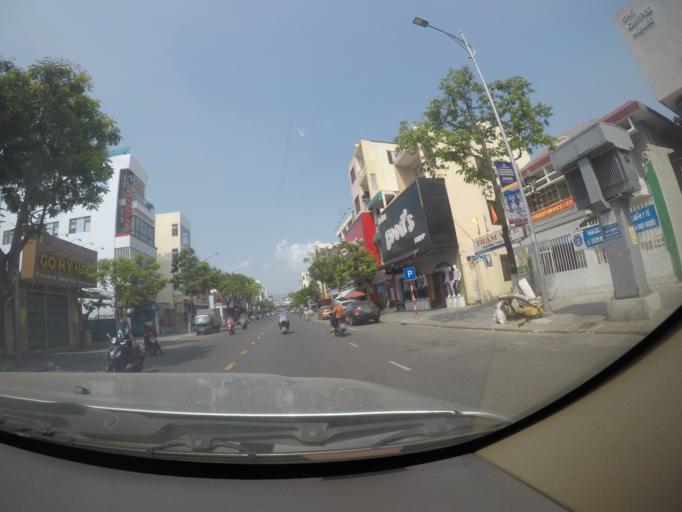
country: VN
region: Da Nang
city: Da Nang
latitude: 16.0671
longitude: 108.2075
